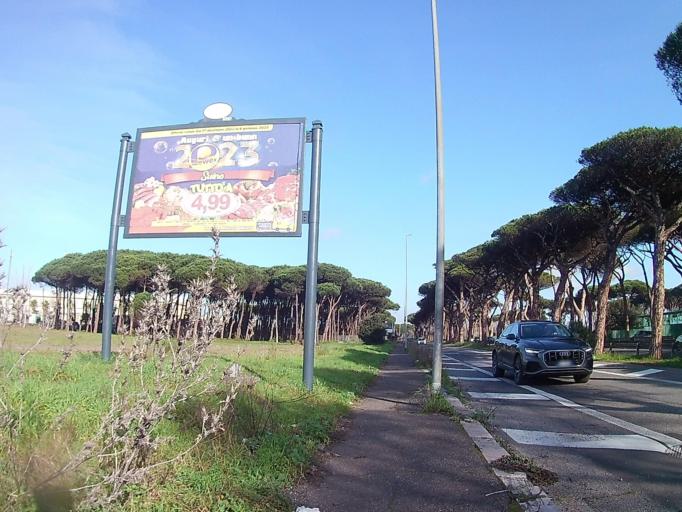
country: IT
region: Latium
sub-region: Citta metropolitana di Roma Capitale
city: Lido di Ostia
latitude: 41.7442
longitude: 12.2867
